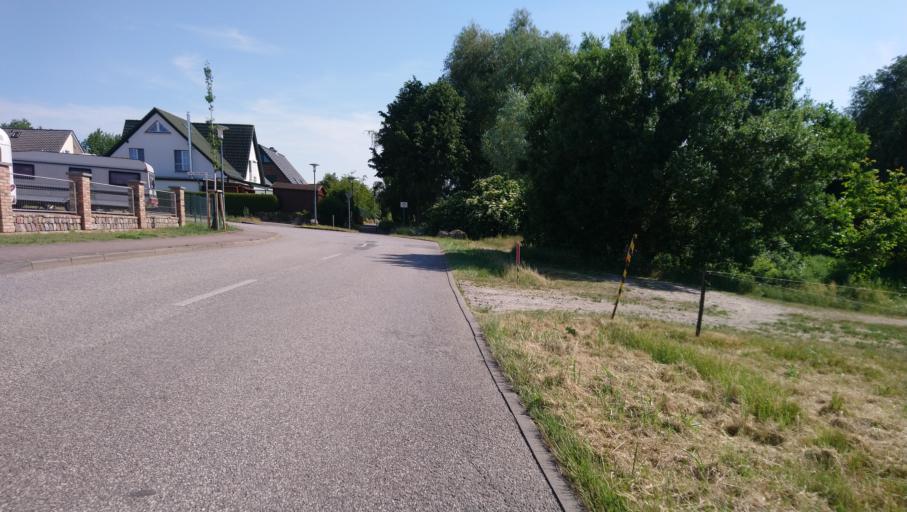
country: DE
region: Mecklenburg-Vorpommern
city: Dierkow-Neu
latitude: 54.0903
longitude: 12.1864
